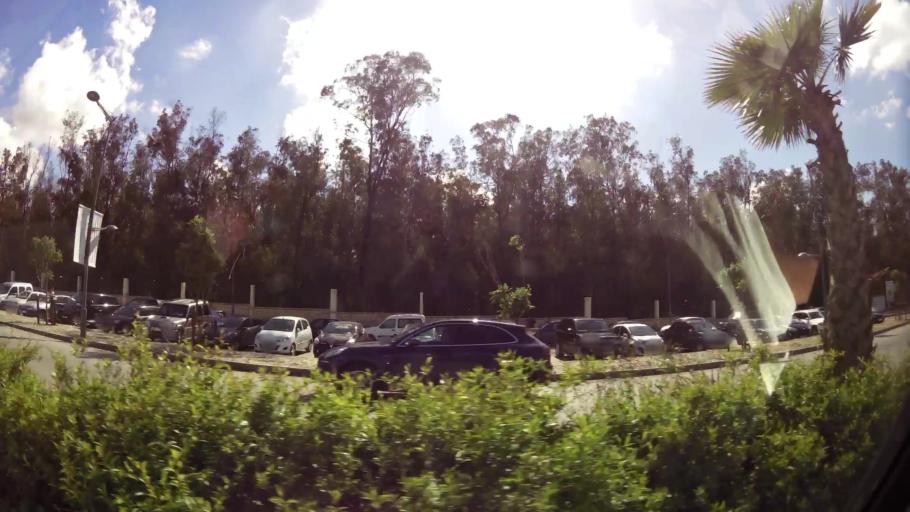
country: MA
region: Grand Casablanca
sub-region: Nouaceur
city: Bouskoura
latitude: 33.4811
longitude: -7.6241
